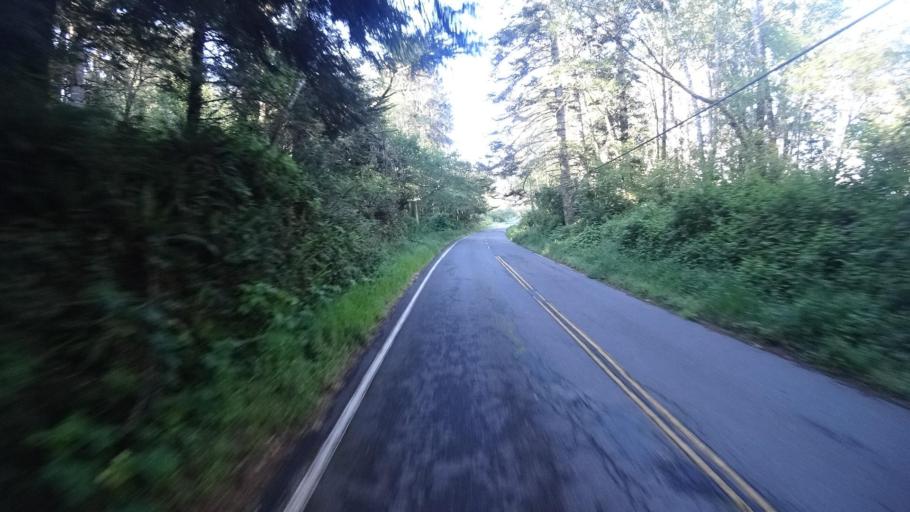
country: US
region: California
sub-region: Humboldt County
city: Westhaven-Moonstone
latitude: 41.1121
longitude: -124.1568
